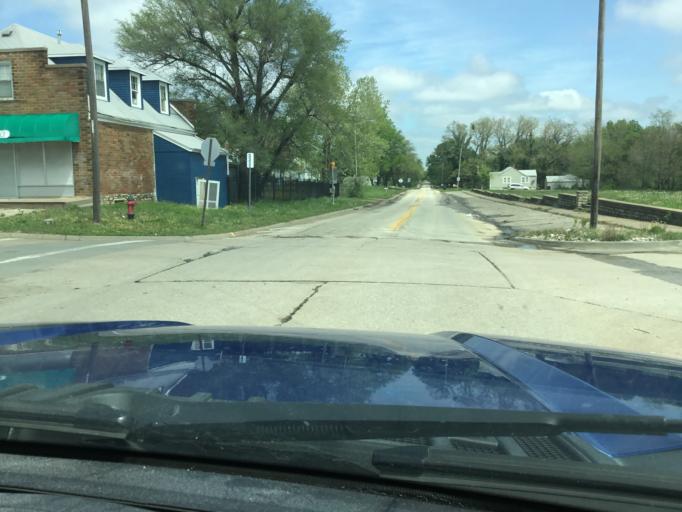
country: US
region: Kansas
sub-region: Shawnee County
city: Topeka
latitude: 39.0189
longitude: -95.6608
